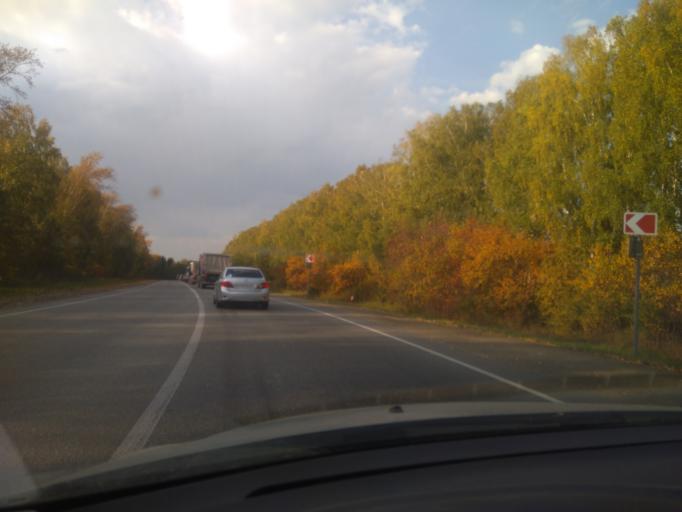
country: RU
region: Sverdlovsk
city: Sovkhoznyy
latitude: 56.5974
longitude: 61.3031
